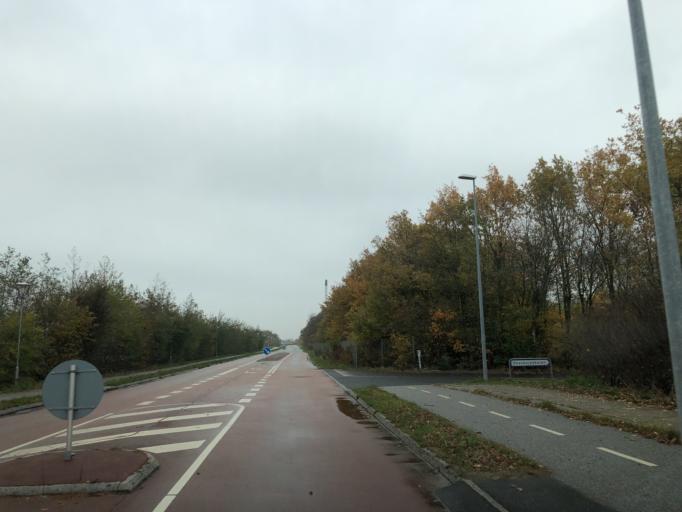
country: DK
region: Central Jutland
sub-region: Herning Kommune
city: Sunds
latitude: 56.2064
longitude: 8.9959
